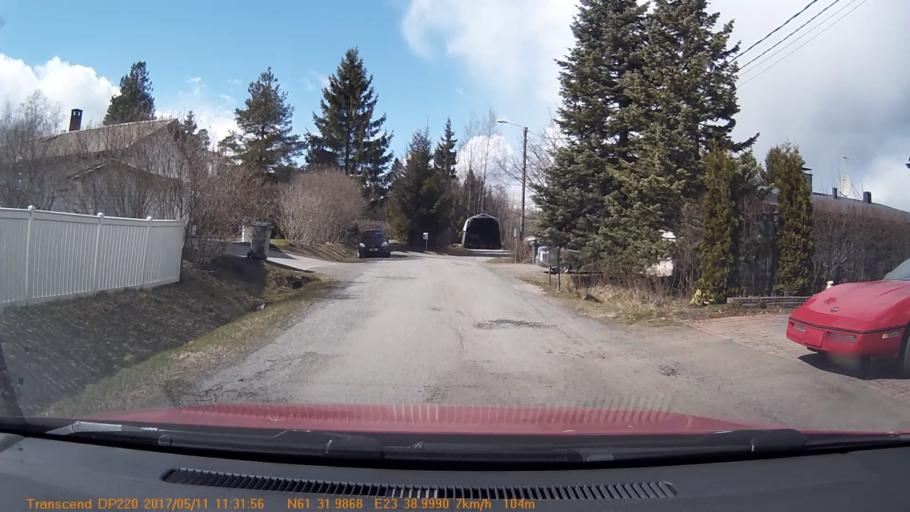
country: FI
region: Pirkanmaa
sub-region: Tampere
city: Yloejaervi
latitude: 61.5331
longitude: 23.6498
